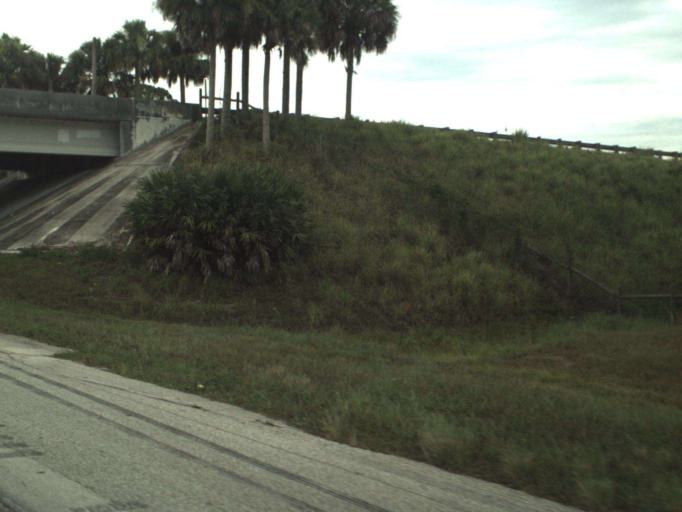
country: US
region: Florida
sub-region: Martin County
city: Palm City
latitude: 27.1267
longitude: -80.3195
